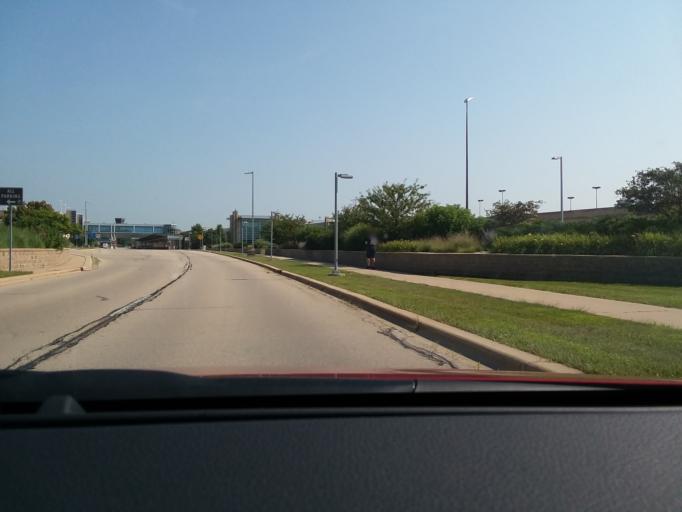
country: US
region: Wisconsin
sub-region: Dane County
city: Maple Bluff
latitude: 43.1334
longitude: -89.3466
